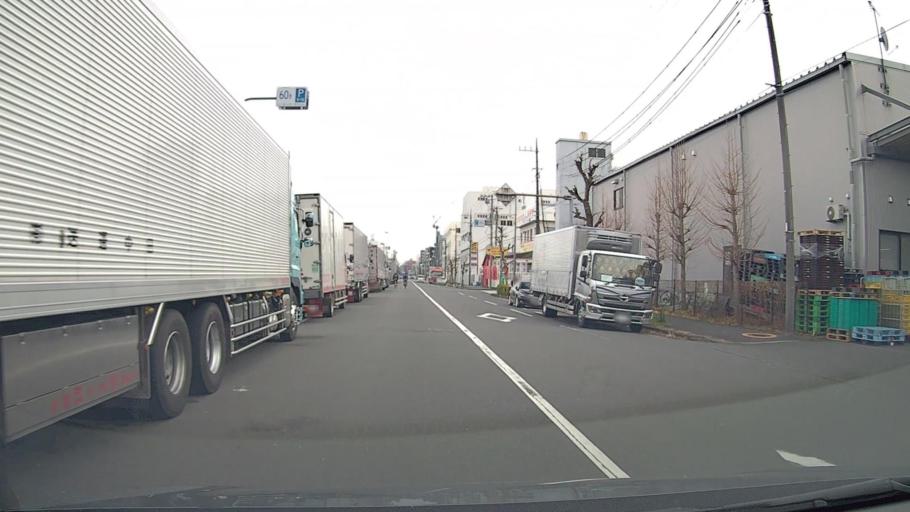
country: JP
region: Saitama
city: Wako
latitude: 35.7925
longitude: 139.6508
